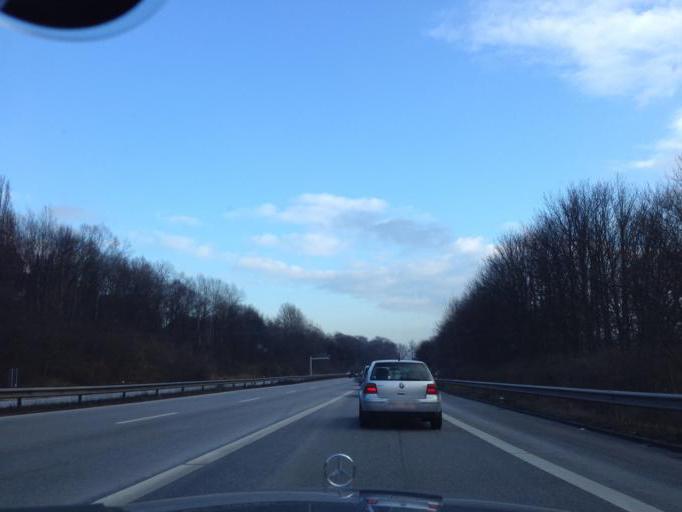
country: DE
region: Hamburg
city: Wandsbek
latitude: 53.5377
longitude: 10.1031
